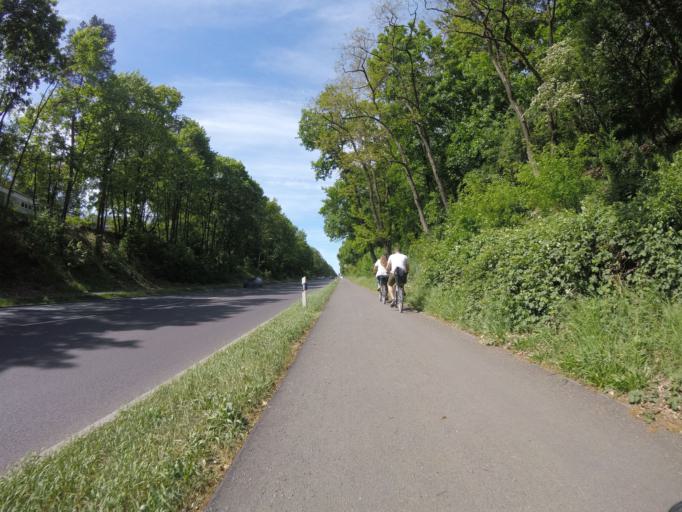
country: DE
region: Berlin
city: Wannsee
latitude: 52.4161
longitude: 13.1289
